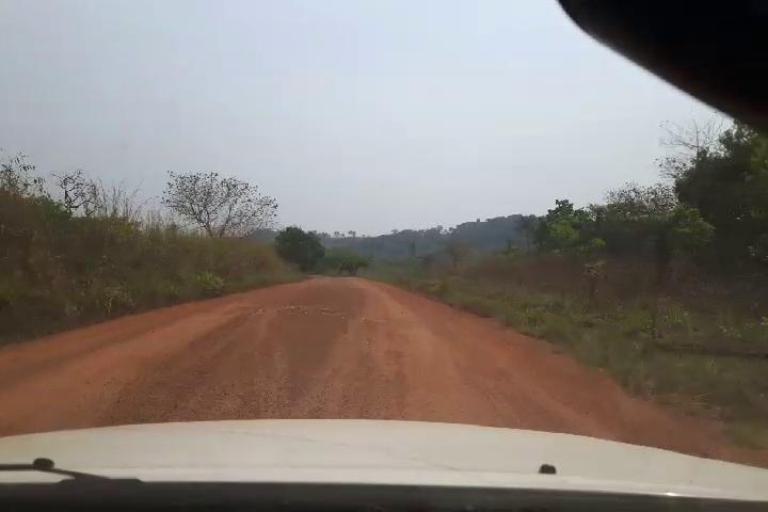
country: SL
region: Northern Province
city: Bumbuna
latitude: 8.9415
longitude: -11.8163
